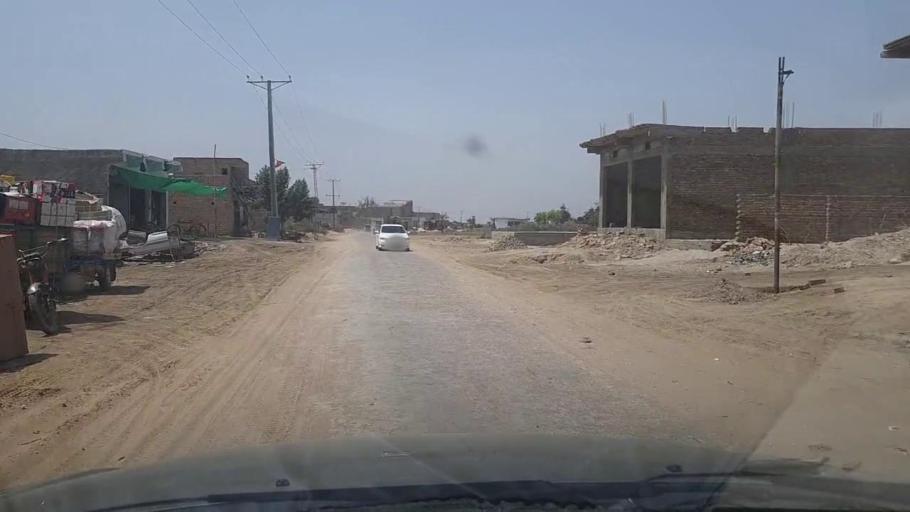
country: PK
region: Sindh
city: Bhiria
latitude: 26.8854
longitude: 68.2703
